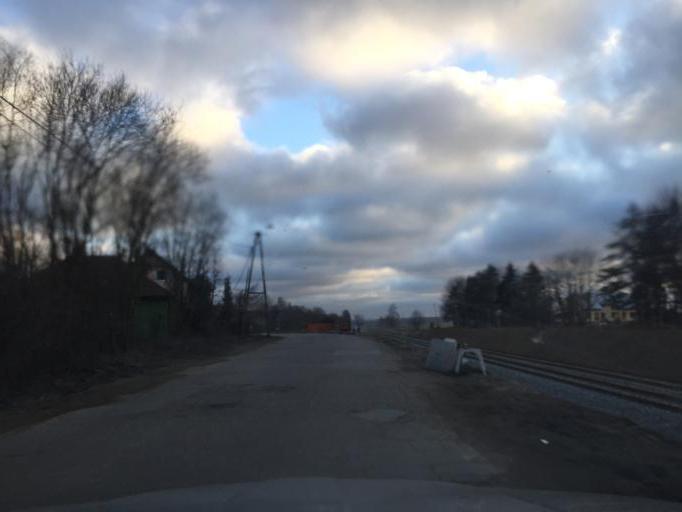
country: PL
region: Pomeranian Voivodeship
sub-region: Powiat kartuski
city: Chwaszczyno
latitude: 54.4145
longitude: 18.4465
